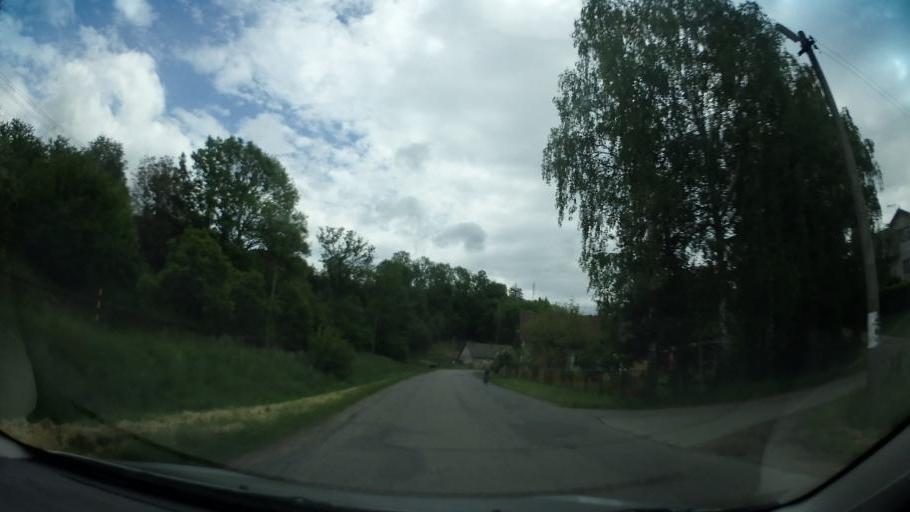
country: CZ
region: Pardubicky
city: Kuncina
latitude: 49.8371
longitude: 16.7012
